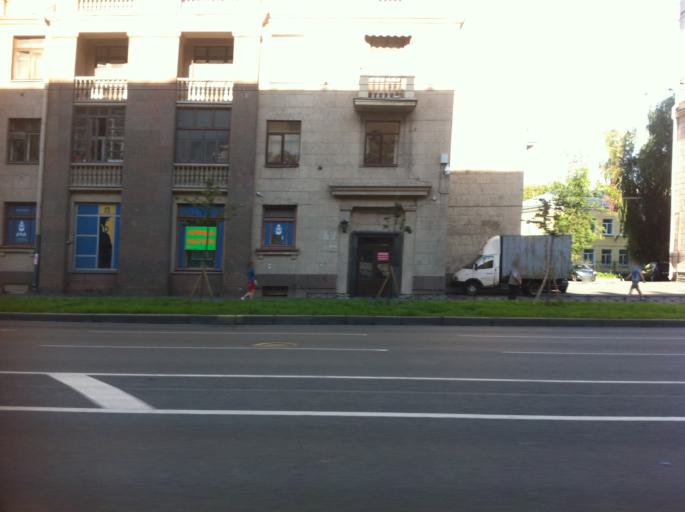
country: RU
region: St.-Petersburg
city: Avtovo
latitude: 59.8724
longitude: 30.2589
